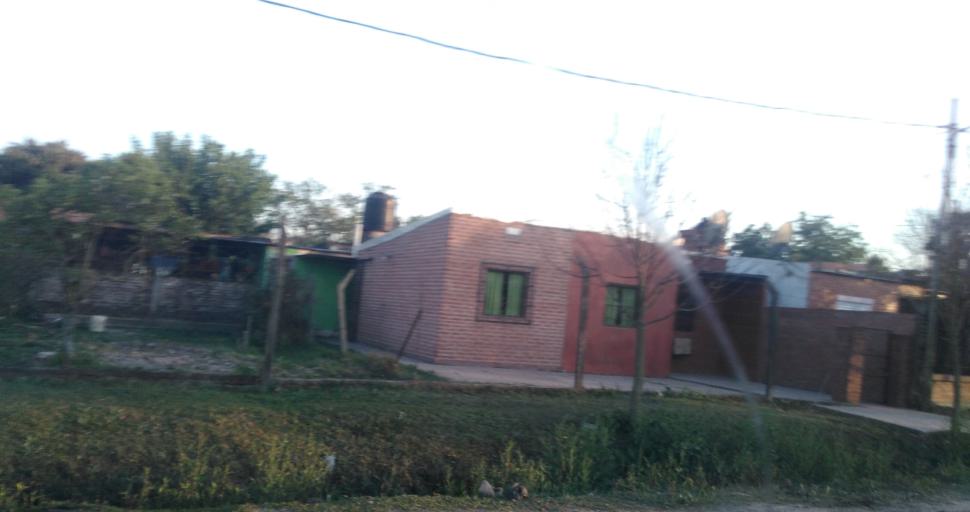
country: AR
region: Chaco
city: Resistencia
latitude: -27.4893
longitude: -59.0006
